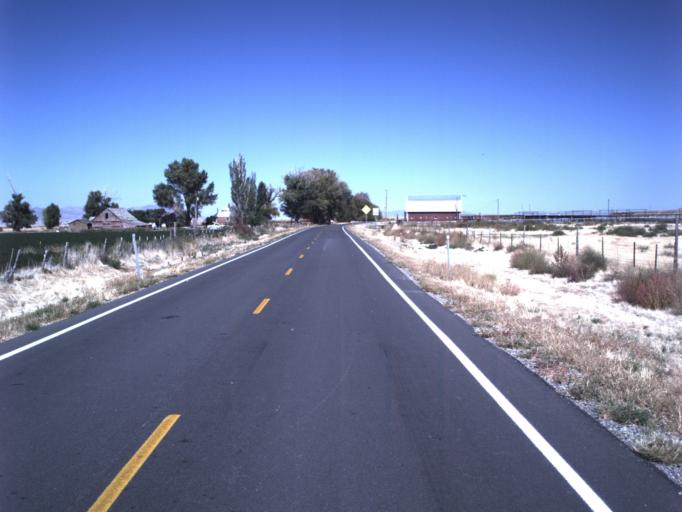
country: US
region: Utah
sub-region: Tooele County
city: Grantsville
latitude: 40.4904
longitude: -112.7472
